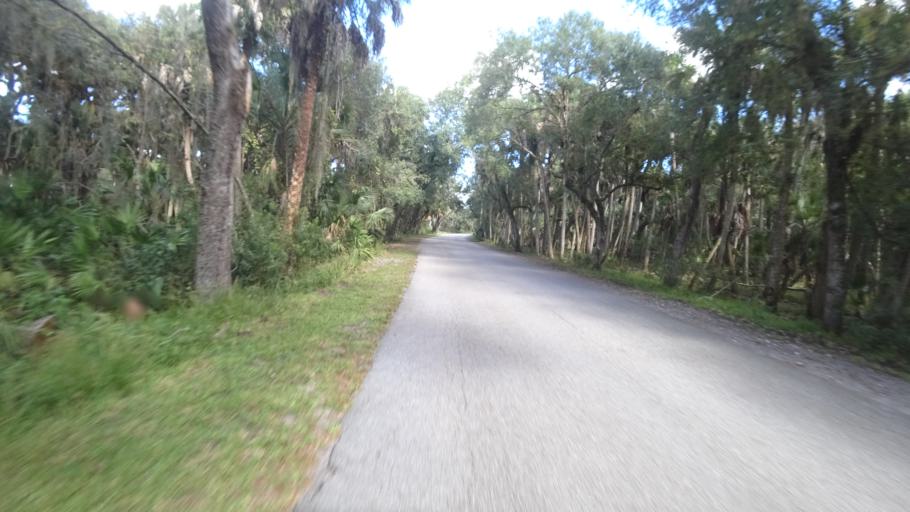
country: US
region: Florida
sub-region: Sarasota County
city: Lake Sarasota
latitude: 27.2458
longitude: -82.3046
